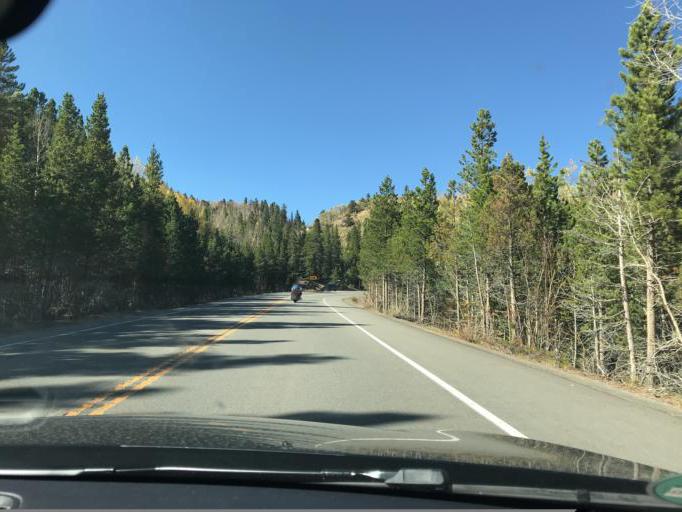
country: US
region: Colorado
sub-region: Boulder County
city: Nederland
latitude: 40.0676
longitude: -105.5161
